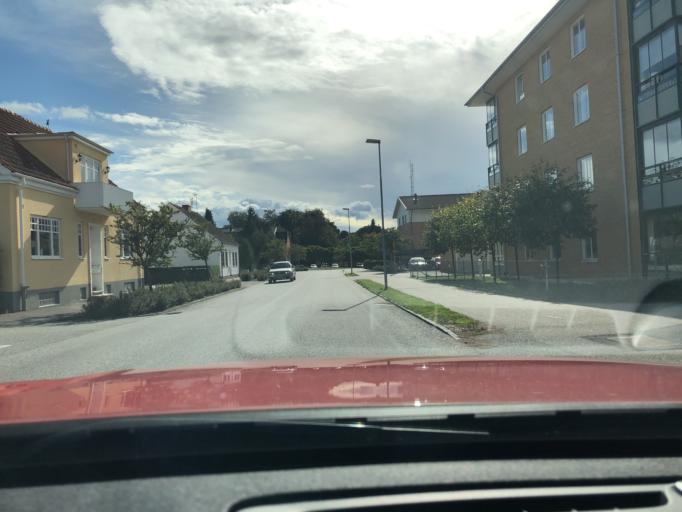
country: SE
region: Skane
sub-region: Sjobo Kommun
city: Sjoebo
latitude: 55.6346
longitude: 13.7039
